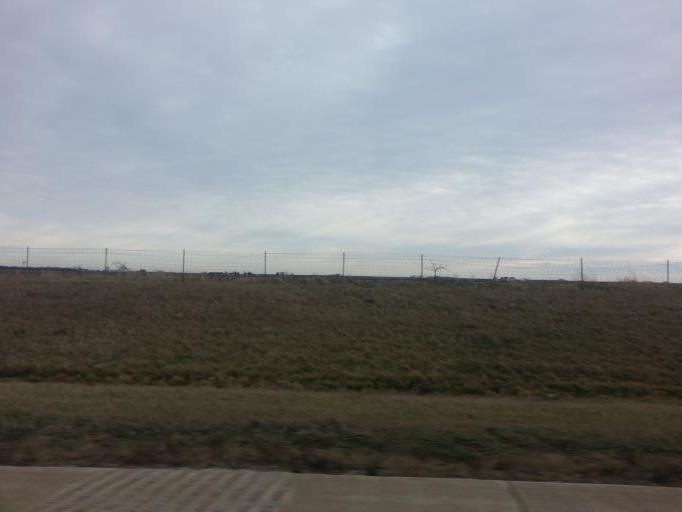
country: US
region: Illinois
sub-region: Woodford County
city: El Paso
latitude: 40.7154
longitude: -89.0335
